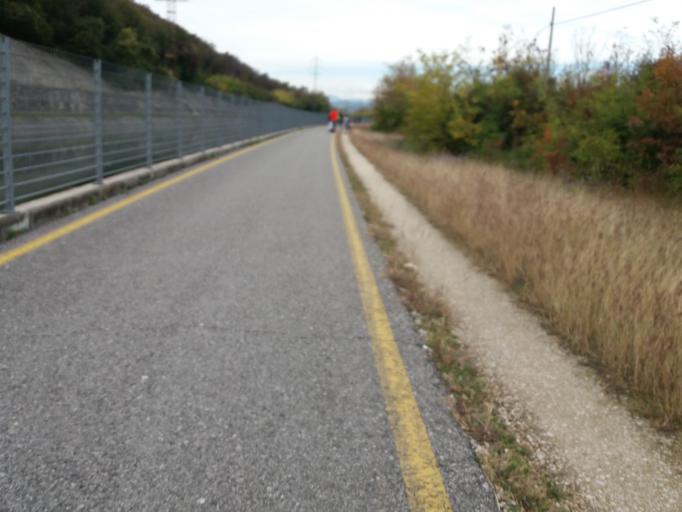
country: IT
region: Veneto
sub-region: Provincia di Verona
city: Pastrengo
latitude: 45.4910
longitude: 10.8172
